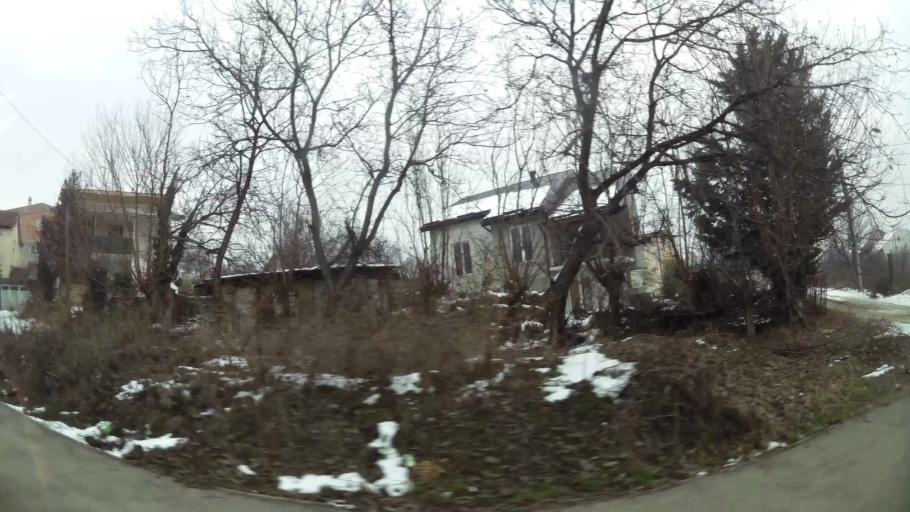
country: MK
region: Saraj
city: Saraj
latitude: 42.0325
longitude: 21.3435
